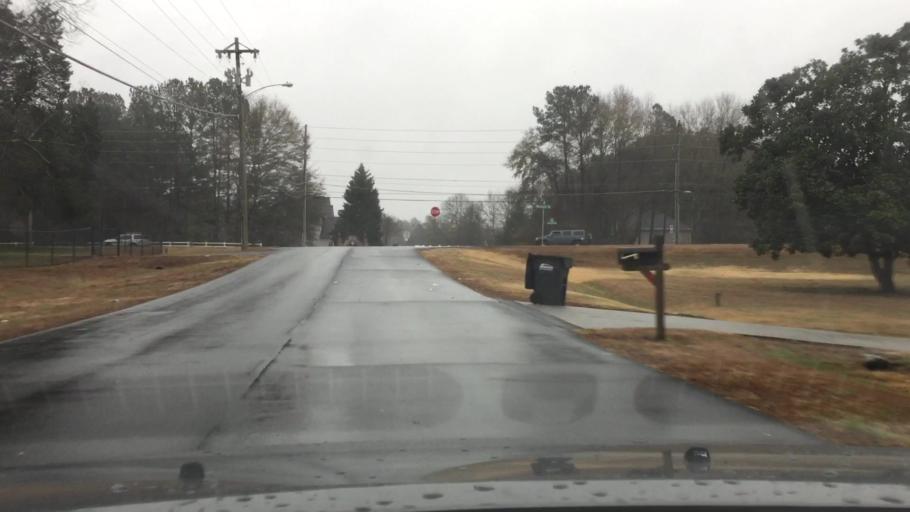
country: US
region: Georgia
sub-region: Cobb County
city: Fair Oaks
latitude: 33.9032
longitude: -84.6199
